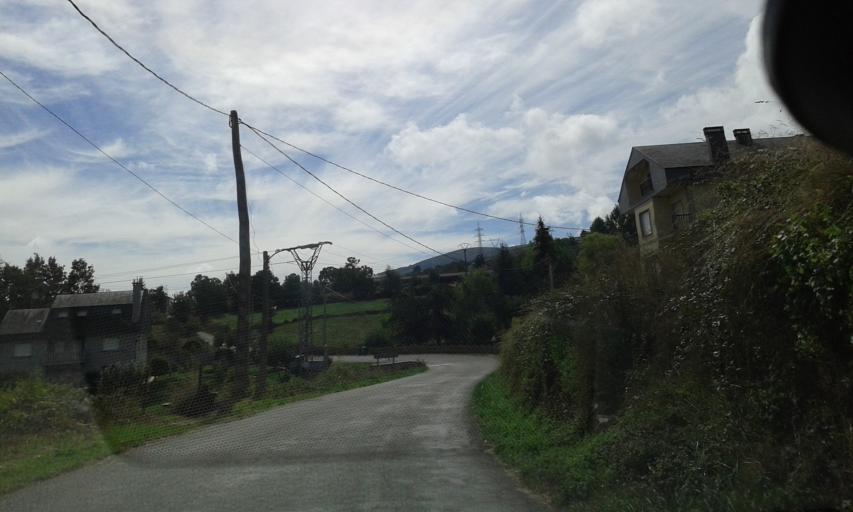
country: ES
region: Galicia
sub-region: Provincia de Ourense
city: Manzaneda
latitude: 42.3069
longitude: -7.2306
